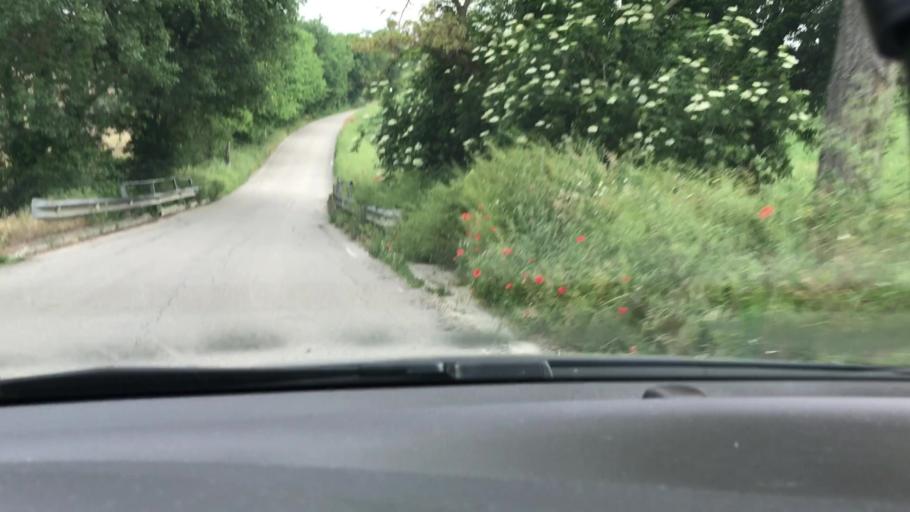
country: IT
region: The Marches
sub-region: Provincia di Macerata
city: Macerata
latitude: 43.2730
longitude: 13.4499
